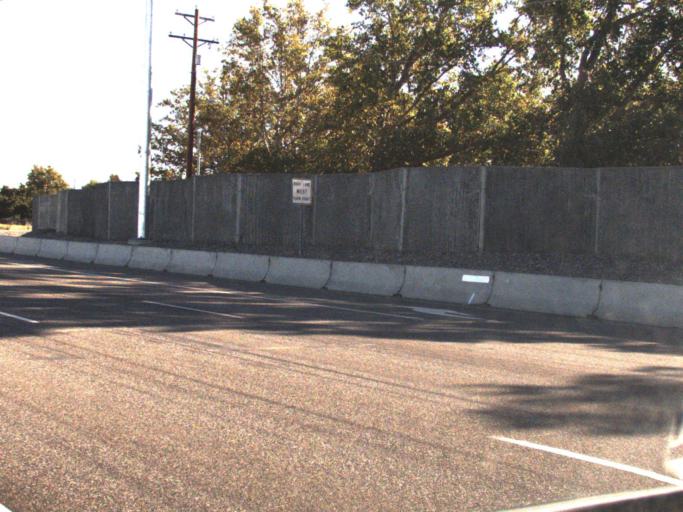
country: US
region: Washington
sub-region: Benton County
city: Richland
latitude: 46.3082
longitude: -119.2864
